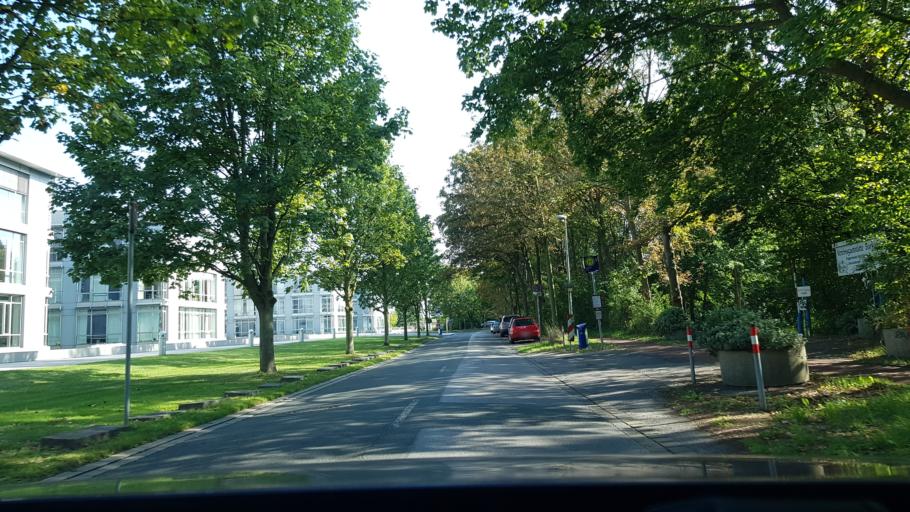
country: DE
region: North Rhine-Westphalia
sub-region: Regierungsbezirk Dusseldorf
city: Duisburg
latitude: 51.4096
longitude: 6.7943
